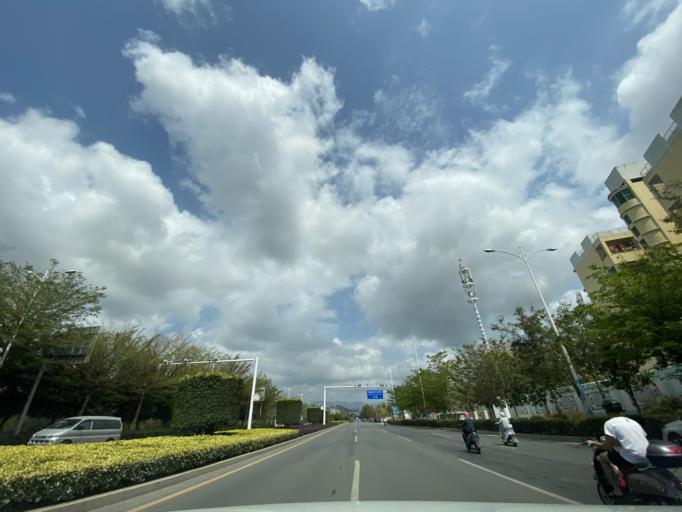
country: CN
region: Hainan
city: Tiandu
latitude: 18.3181
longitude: 109.5264
